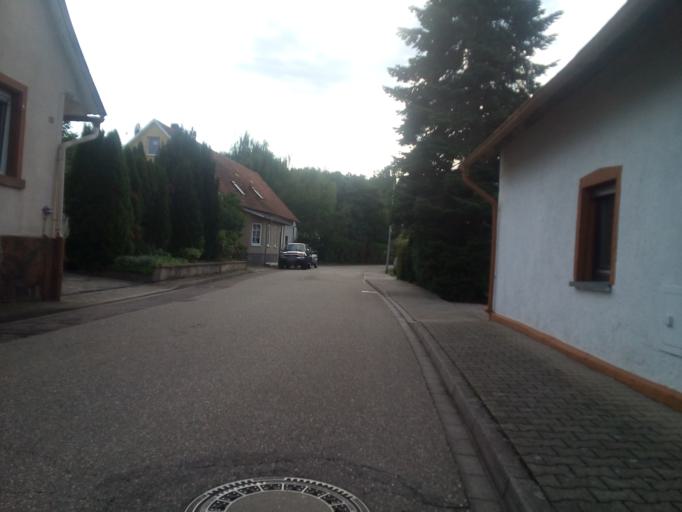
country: DE
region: Baden-Wuerttemberg
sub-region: Karlsruhe Region
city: Schwarzach
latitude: 48.7348
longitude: 8.0572
